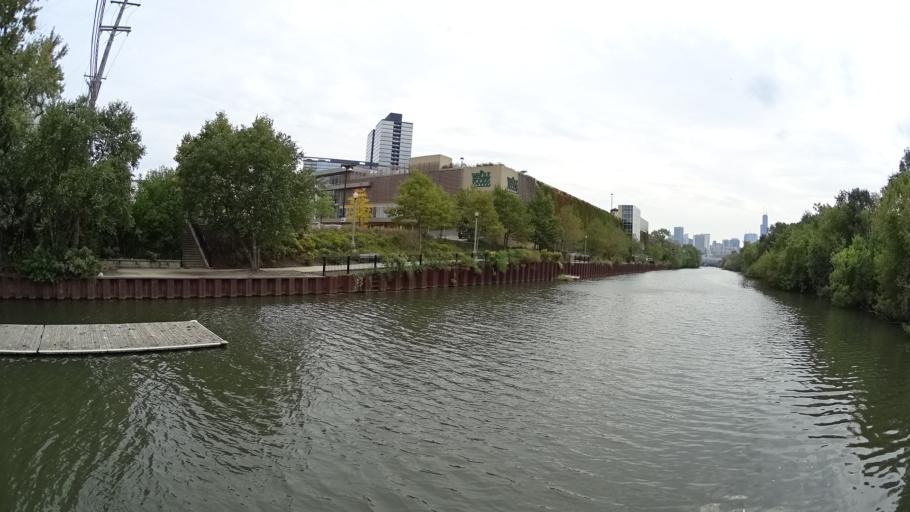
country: US
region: Illinois
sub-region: Cook County
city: Chicago
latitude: 41.9093
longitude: -87.6543
